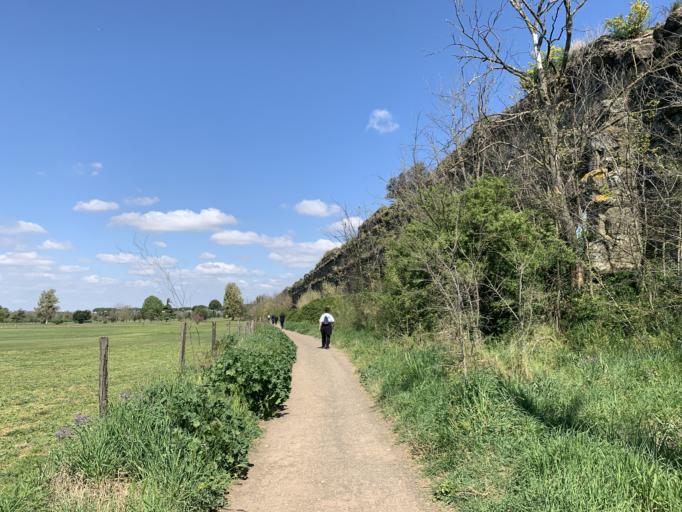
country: IT
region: Latium
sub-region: Citta metropolitana di Roma Capitale
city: Ciampino
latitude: 41.8394
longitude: 12.5678
